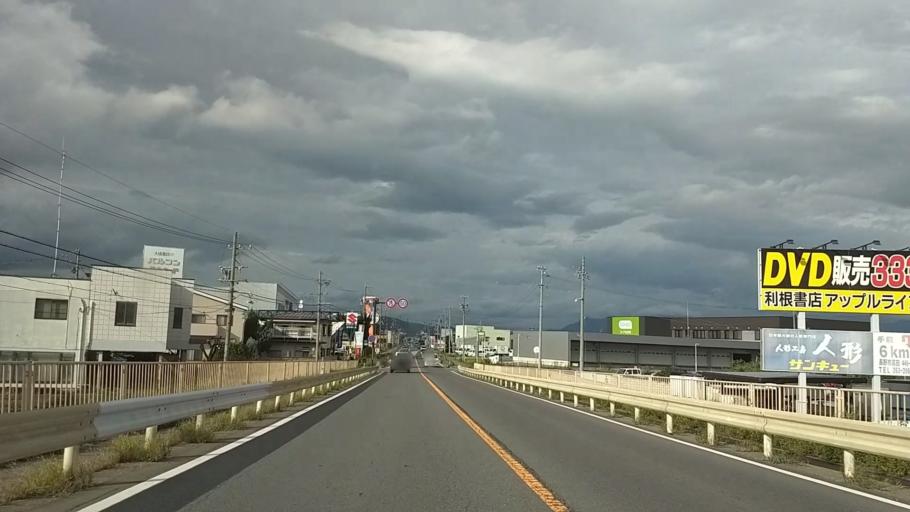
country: JP
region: Nagano
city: Suzaka
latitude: 36.6658
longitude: 138.2630
